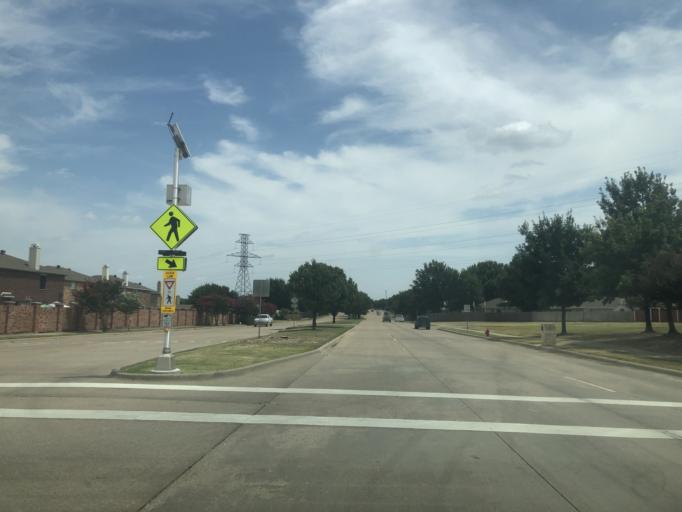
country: US
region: Texas
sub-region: Tarrant County
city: Saginaw
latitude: 32.8762
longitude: -97.3518
